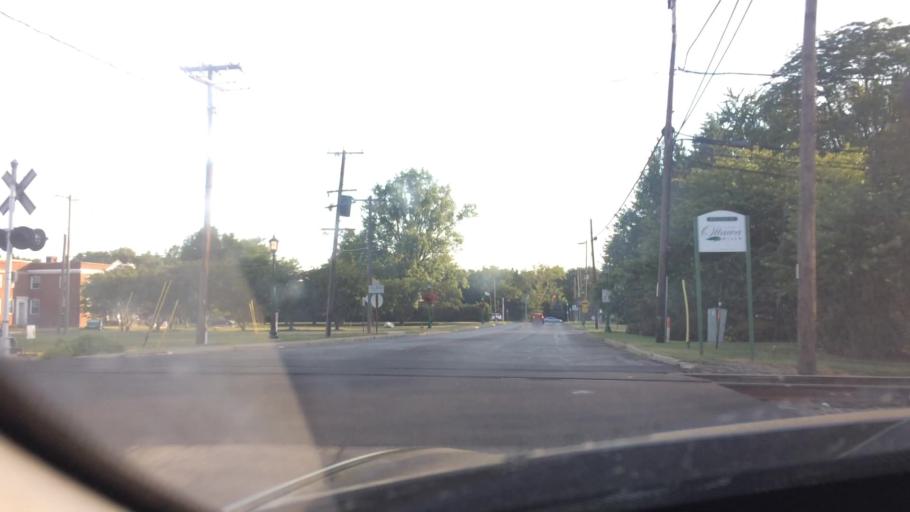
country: US
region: Ohio
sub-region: Lucas County
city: Ottawa Hills
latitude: 41.6607
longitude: -83.6412
